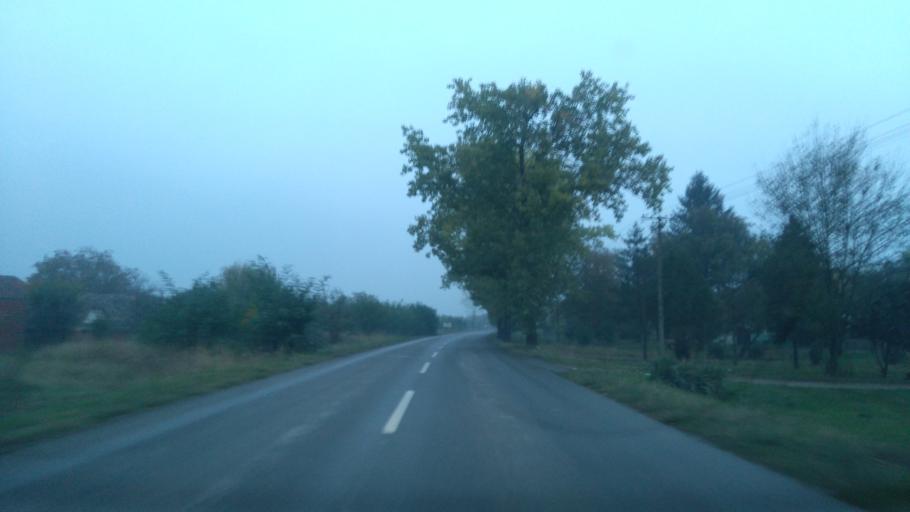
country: RS
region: Autonomna Pokrajina Vojvodina
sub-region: Juznobacki Okrug
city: Becej
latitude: 45.6349
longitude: 20.0305
